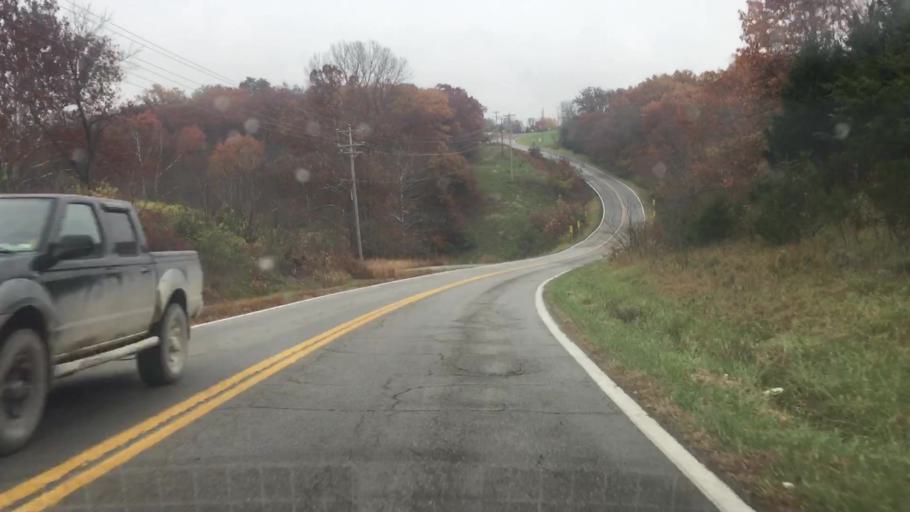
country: US
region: Missouri
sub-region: Callaway County
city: Fulton
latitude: 38.8426
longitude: -91.9268
